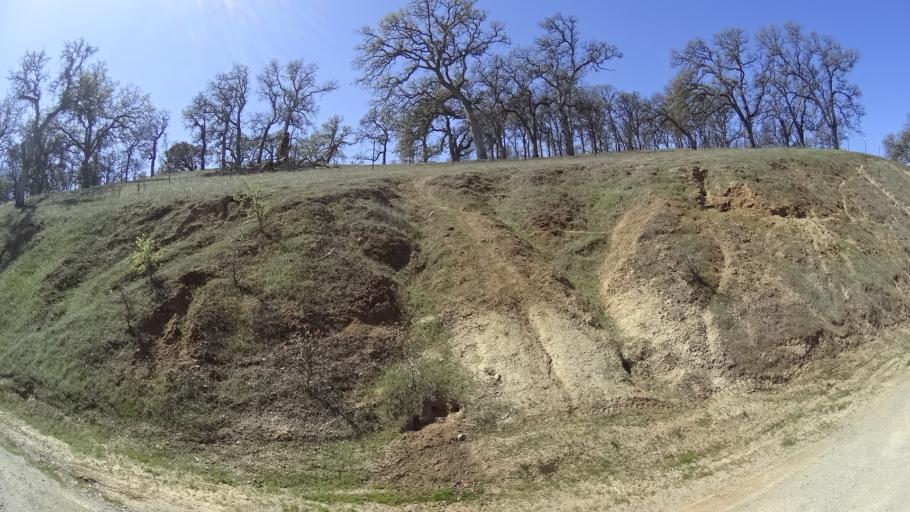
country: US
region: California
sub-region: Glenn County
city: Orland
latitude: 39.7717
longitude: -122.3554
